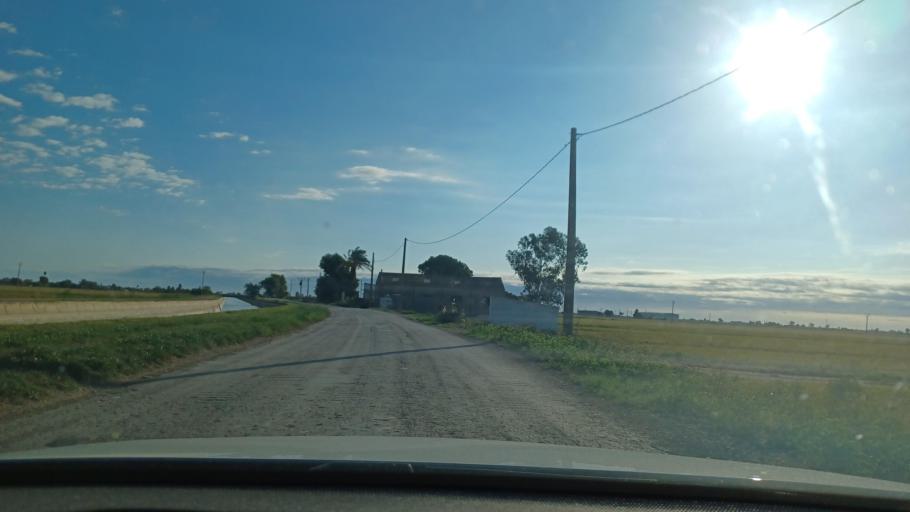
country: ES
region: Catalonia
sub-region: Provincia de Tarragona
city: Amposta
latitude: 40.6990
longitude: 0.6155
